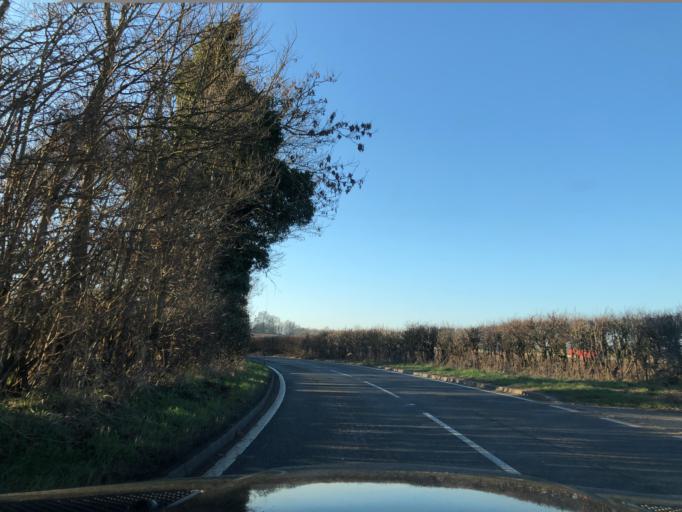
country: GB
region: England
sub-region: Warwickshire
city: Warwick
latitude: 52.2612
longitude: -1.6242
